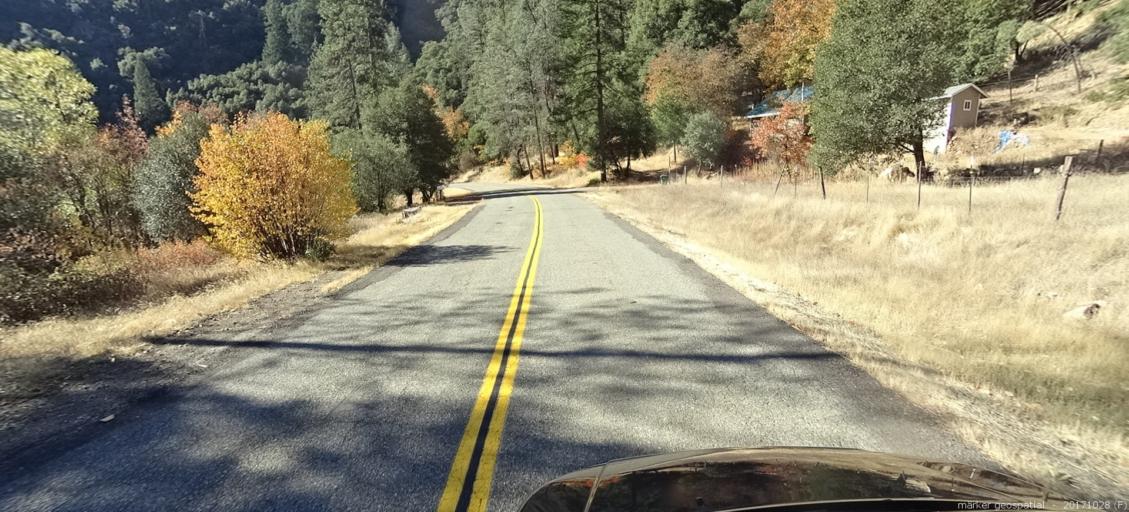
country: US
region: California
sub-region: Trinity County
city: Lewiston
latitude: 40.7757
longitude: -122.6123
